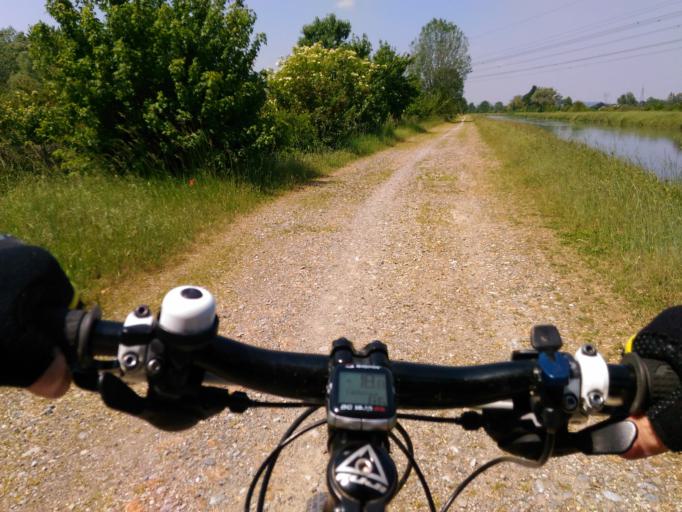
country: IT
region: Lombardy
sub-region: Provincia di Lodi
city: Montanaso Lombardo
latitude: 45.3417
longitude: 9.4785
